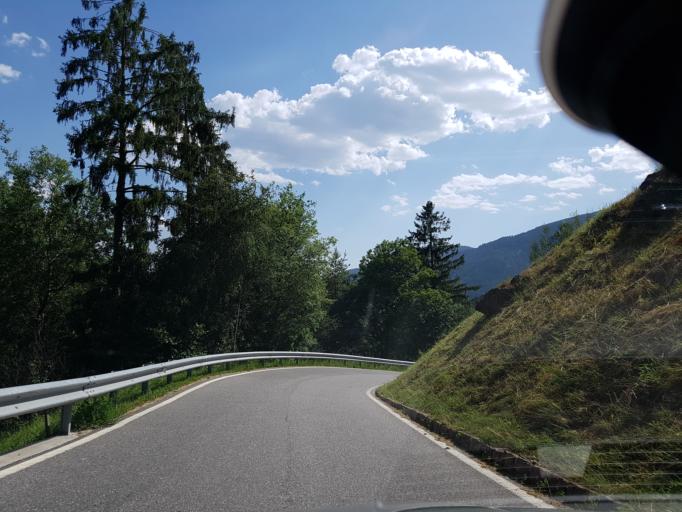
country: IT
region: Trentino-Alto Adige
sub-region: Bolzano
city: Villandro - Villanders
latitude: 46.6387
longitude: 11.5309
